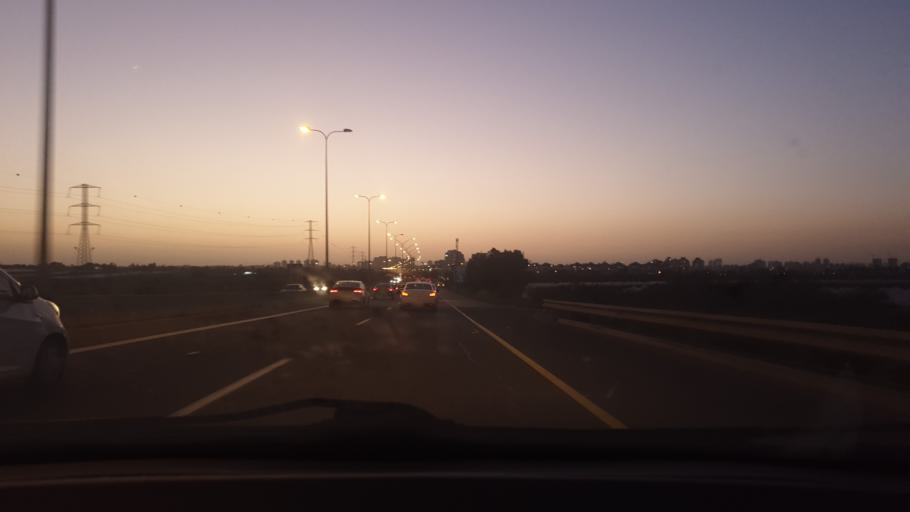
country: IL
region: Central District
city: Nehalim
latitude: 32.0681
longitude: 34.9294
